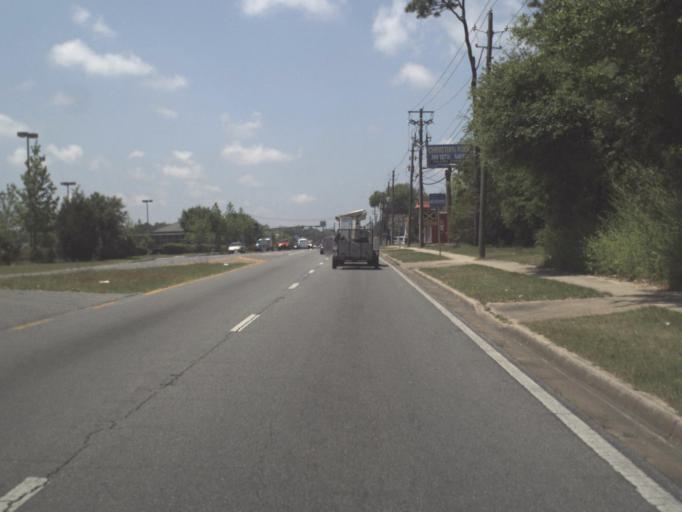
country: US
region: Florida
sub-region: Escambia County
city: West Pensacola
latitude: 30.4356
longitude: -87.2702
